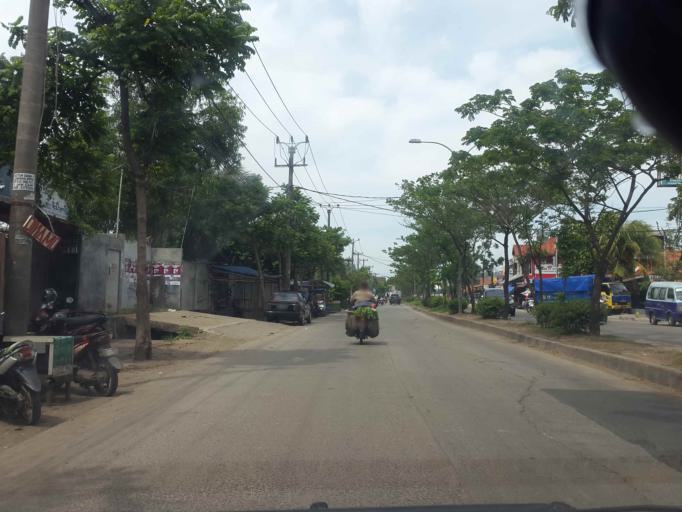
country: ID
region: Banten
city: Tangerang
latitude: -6.1501
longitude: 106.6743
